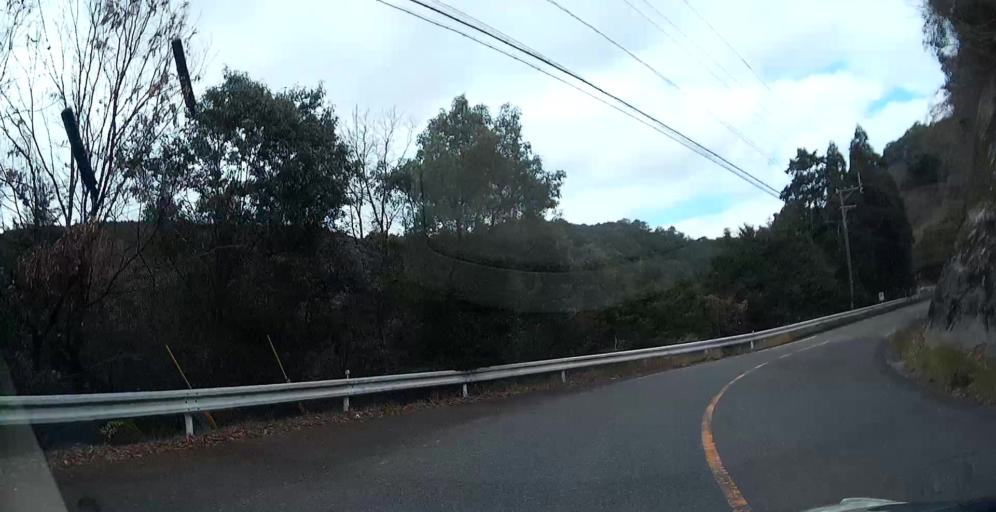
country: JP
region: Kumamoto
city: Yatsushiro
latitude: 32.3672
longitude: 130.5061
